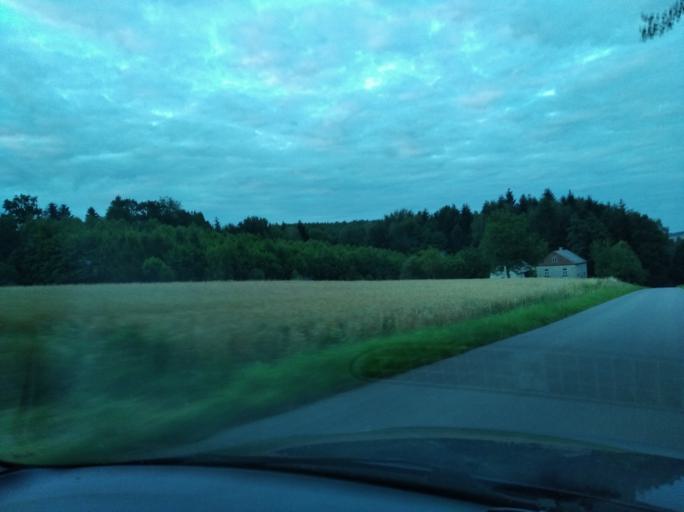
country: PL
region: Subcarpathian Voivodeship
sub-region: Powiat ropczycko-sedziszowski
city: Zagorzyce
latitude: 49.9914
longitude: 21.7106
